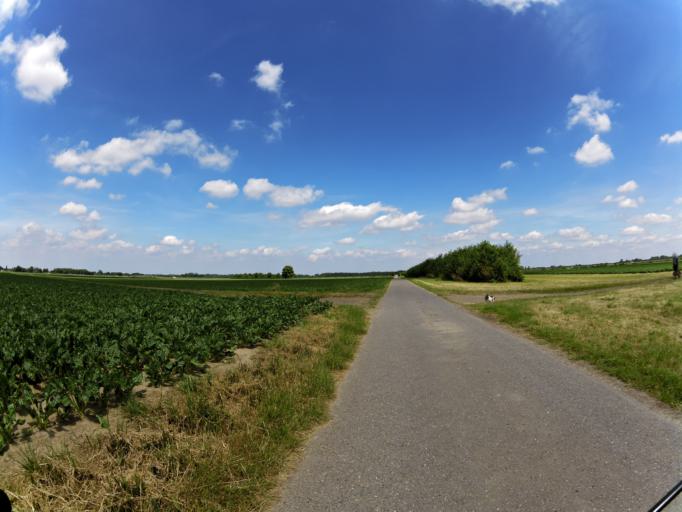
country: NL
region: Limburg
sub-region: Gemeente Sittard-Geleen
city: Sittard
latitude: 51.0224
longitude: 5.8944
